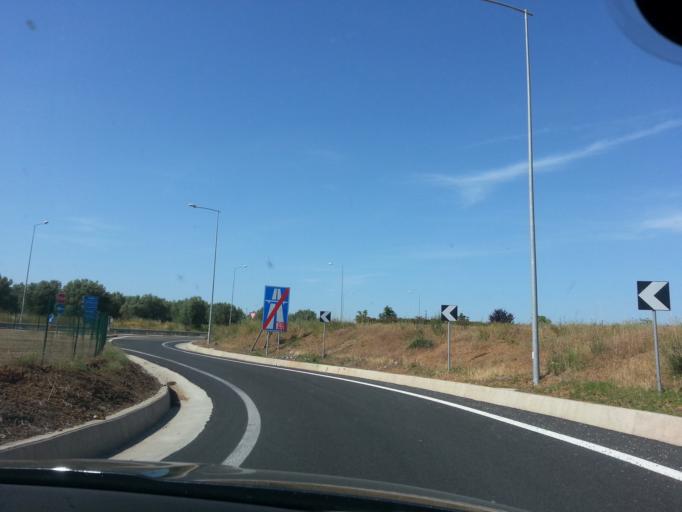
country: IT
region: Latium
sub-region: Provincia di Viterbo
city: Blera
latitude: 42.3072
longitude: 11.9892
